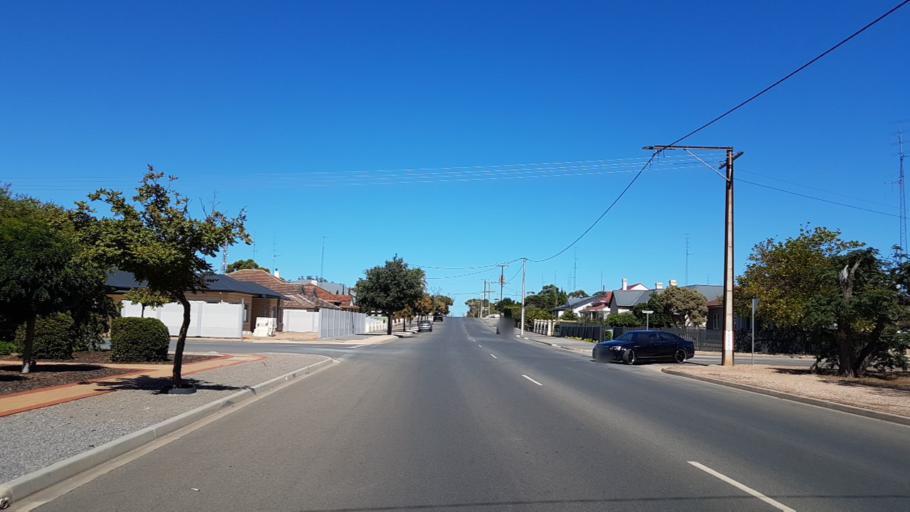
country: AU
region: South Australia
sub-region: Copper Coast
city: Kadina
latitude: -33.9613
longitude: 137.7223
